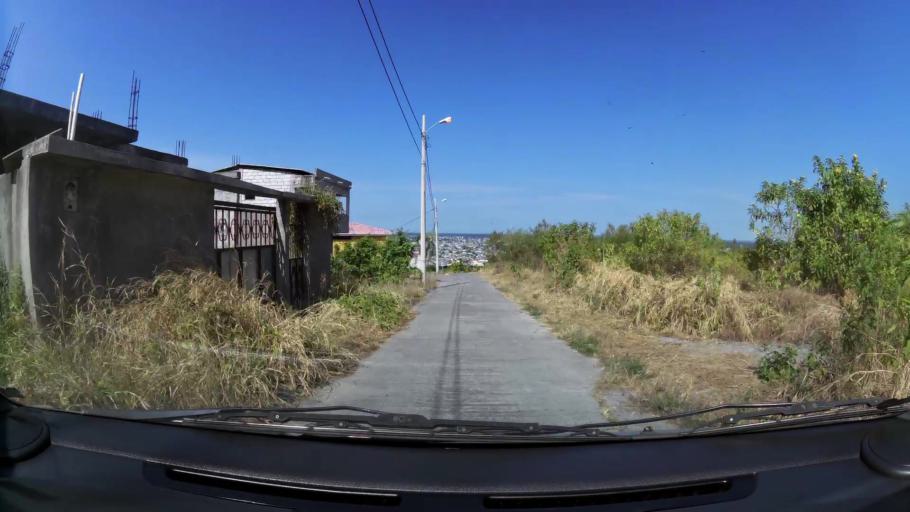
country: EC
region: Guayas
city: Guayaquil
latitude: -2.1839
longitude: -79.9176
